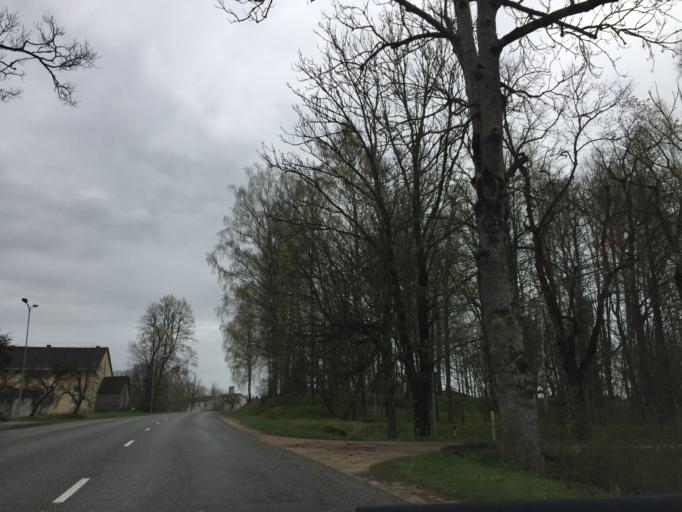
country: LV
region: Sigulda
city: Sigulda
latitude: 57.0255
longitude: 24.8171
